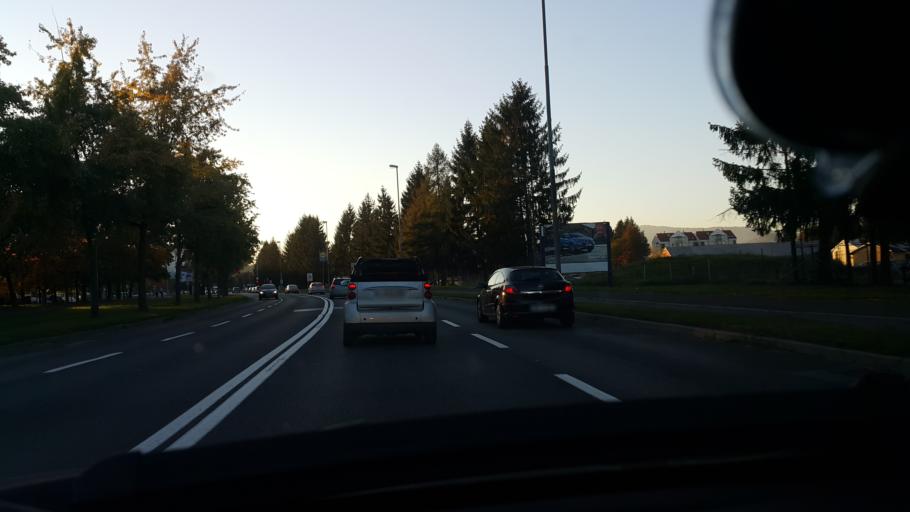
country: SI
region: Maribor
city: Maribor
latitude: 46.5445
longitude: 15.6279
